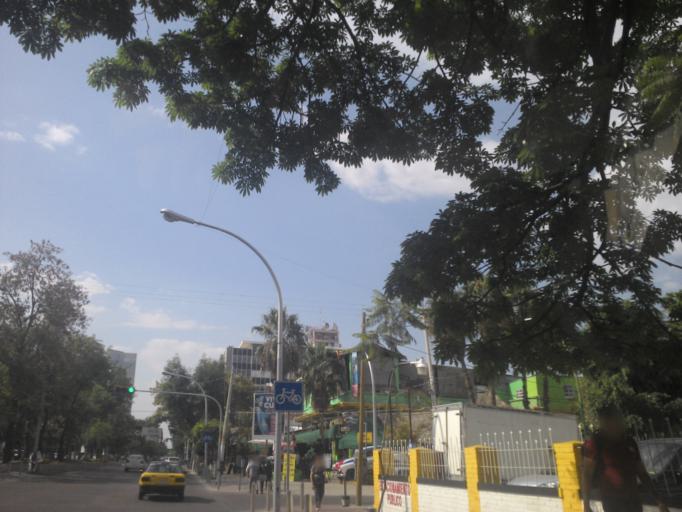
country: MX
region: Jalisco
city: Guadalajara
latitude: 20.6712
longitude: -103.3685
